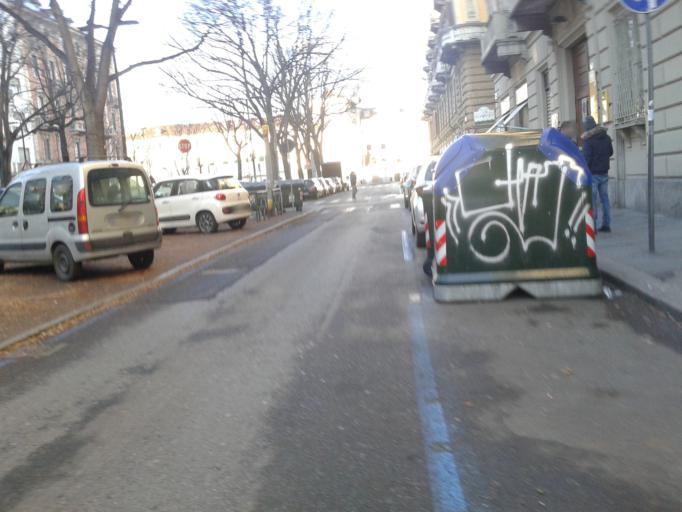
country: IT
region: Piedmont
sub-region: Provincia di Torino
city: Turin
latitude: 45.0567
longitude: 7.6784
